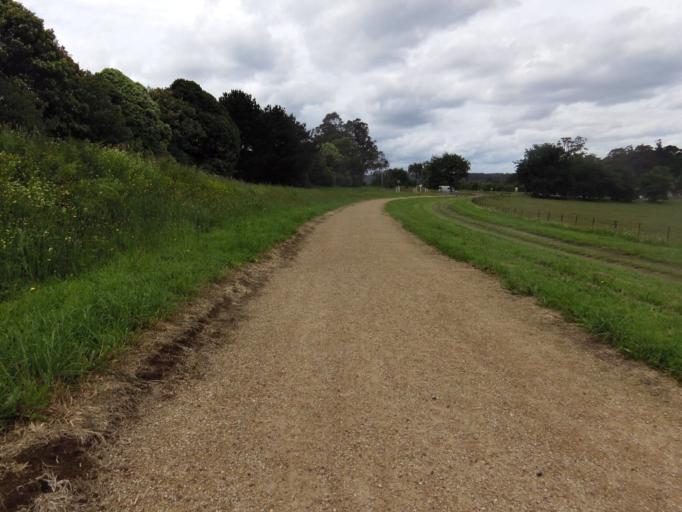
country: AU
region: Victoria
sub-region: Cardinia
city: Gembrook
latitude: -37.9476
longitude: 145.5348
